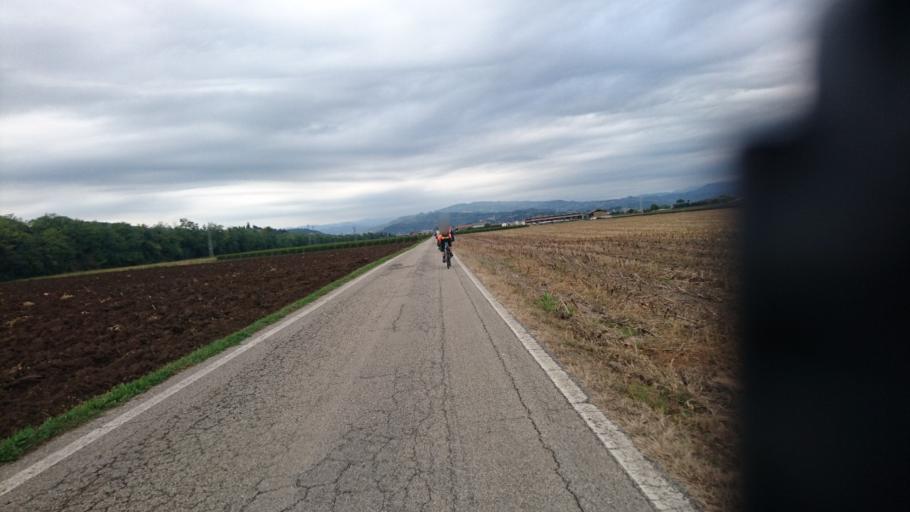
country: IT
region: Veneto
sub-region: Provincia di Vicenza
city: Zermeghedo
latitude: 45.4832
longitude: 11.3805
